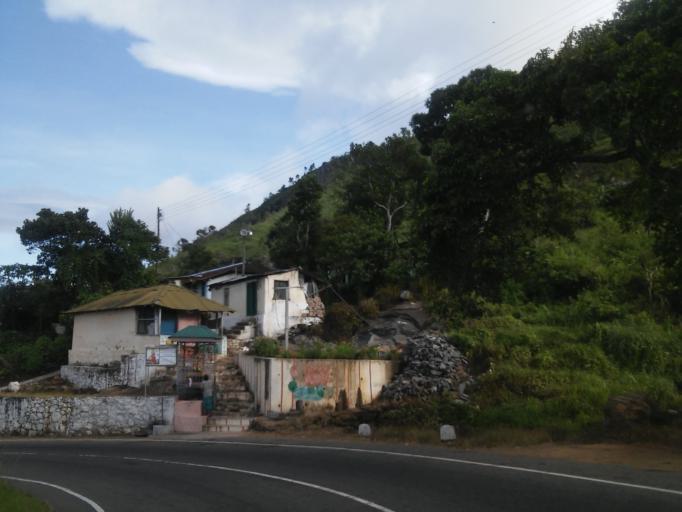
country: LK
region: Uva
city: Haputale
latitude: 6.7595
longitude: 80.9411
